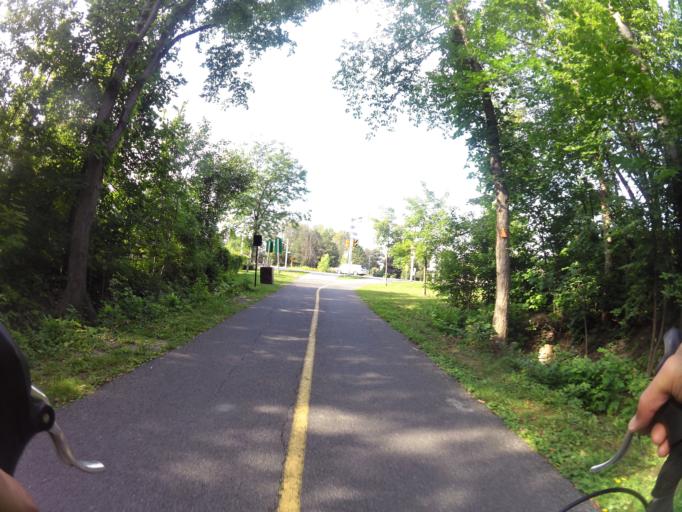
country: CA
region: Ontario
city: Bells Corners
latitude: 45.3474
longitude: -75.8164
